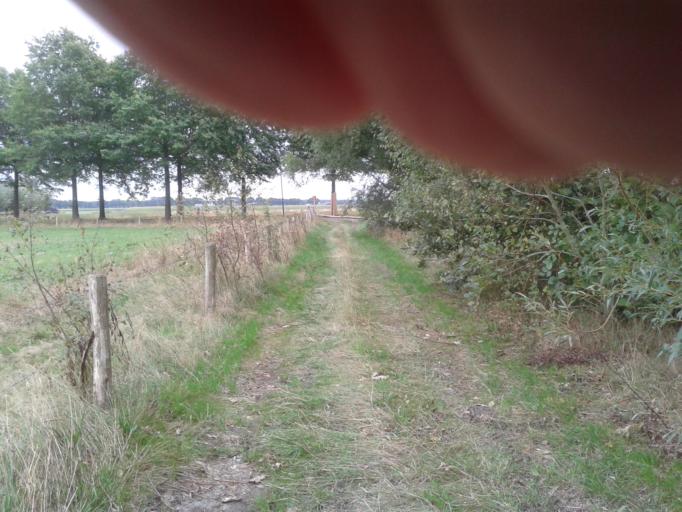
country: NL
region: North Brabant
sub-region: Gemeente Hilvarenbeek
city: Hilvarenbeek
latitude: 51.5143
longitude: 5.1946
